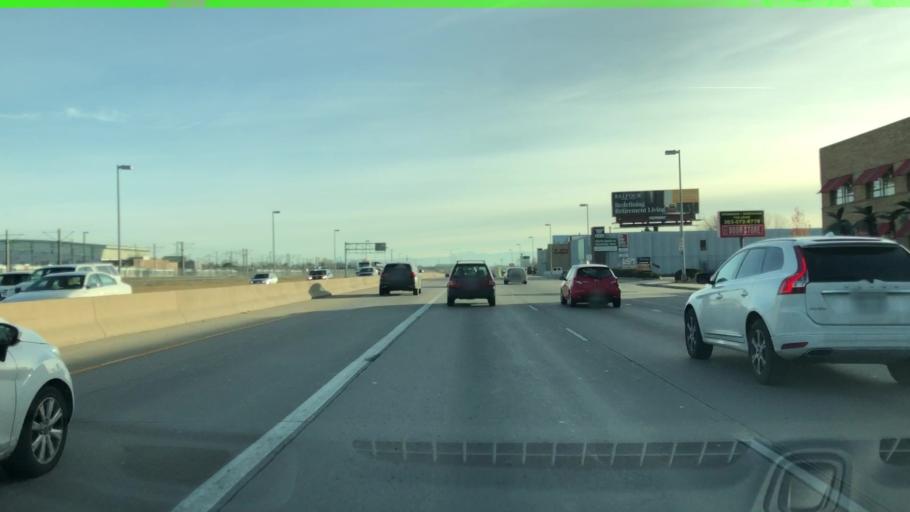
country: US
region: Colorado
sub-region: Arapahoe County
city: Englewood
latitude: 39.6705
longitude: -104.9955
